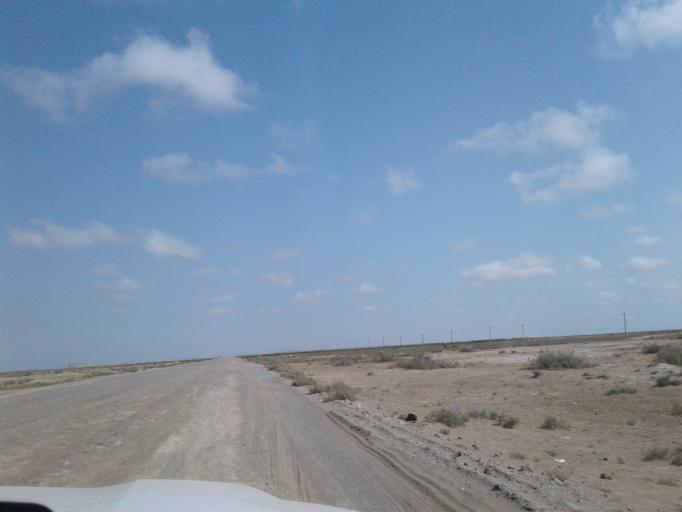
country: IR
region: Golestan
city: Gomishan
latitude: 37.6582
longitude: 53.9330
